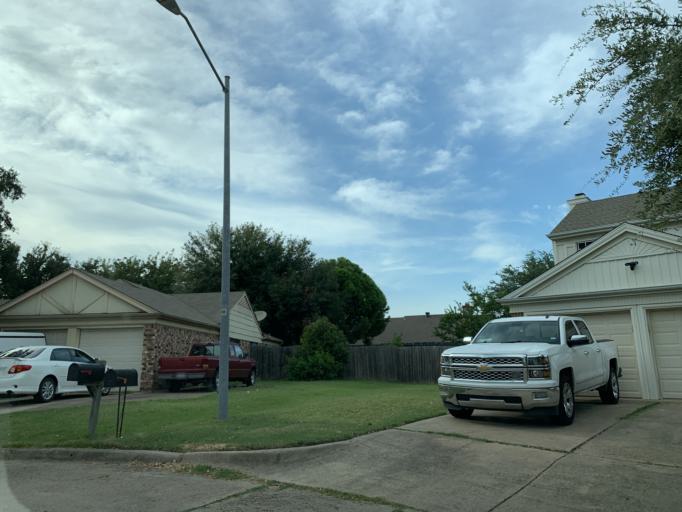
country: US
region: Texas
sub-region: Dallas County
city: Grand Prairie
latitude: 32.6612
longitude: -97.0436
